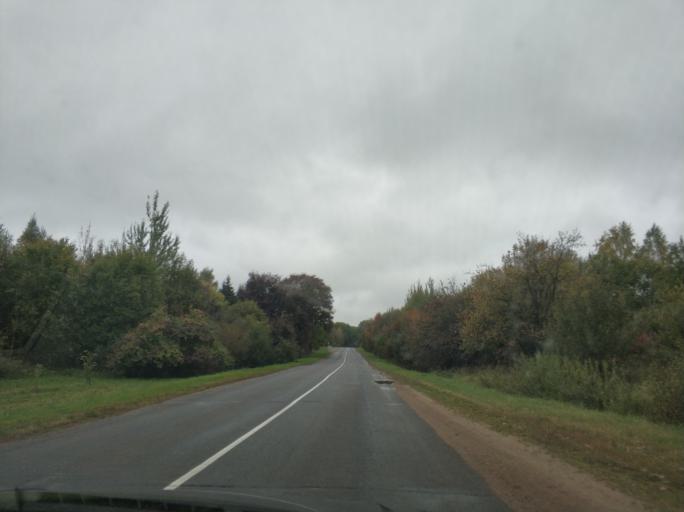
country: BY
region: Vitebsk
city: Polatsk
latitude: 55.4433
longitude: 28.9493
